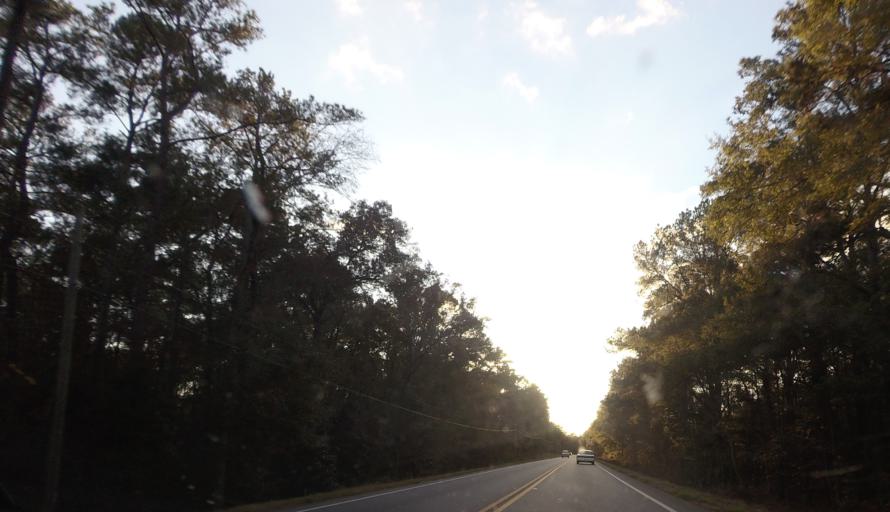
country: US
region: Georgia
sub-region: Houston County
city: Robins Air Force Base
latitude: 32.5421
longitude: -83.4442
